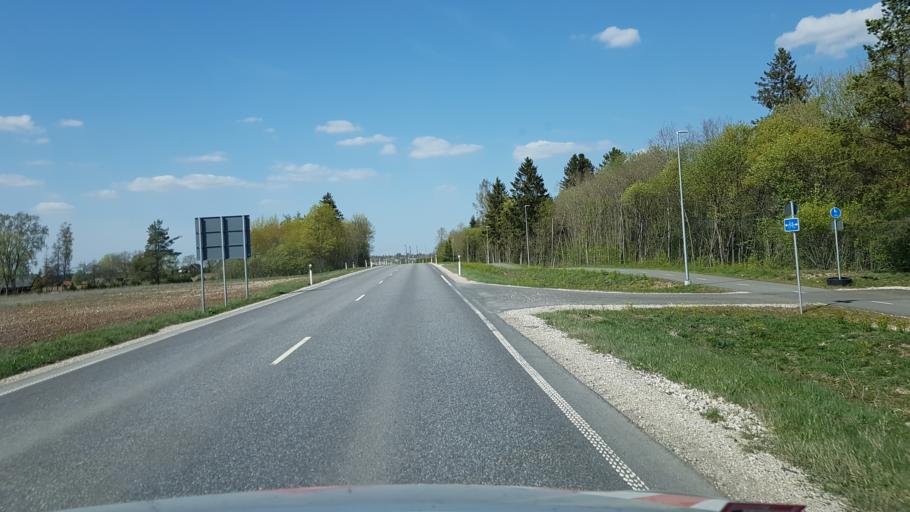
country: EE
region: Harju
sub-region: Raasiku vald
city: Arukula
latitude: 59.1873
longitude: 25.1150
